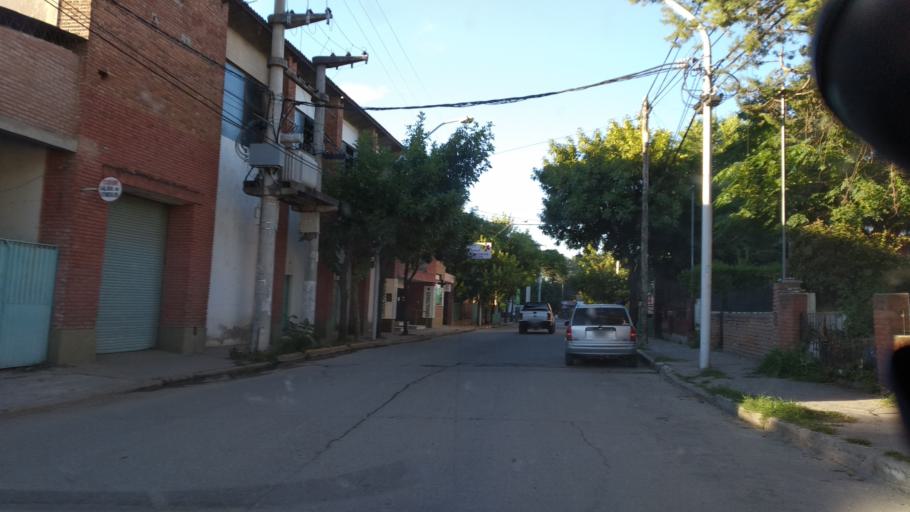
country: AR
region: Cordoba
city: Mina Clavero
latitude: -31.7162
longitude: -65.0060
